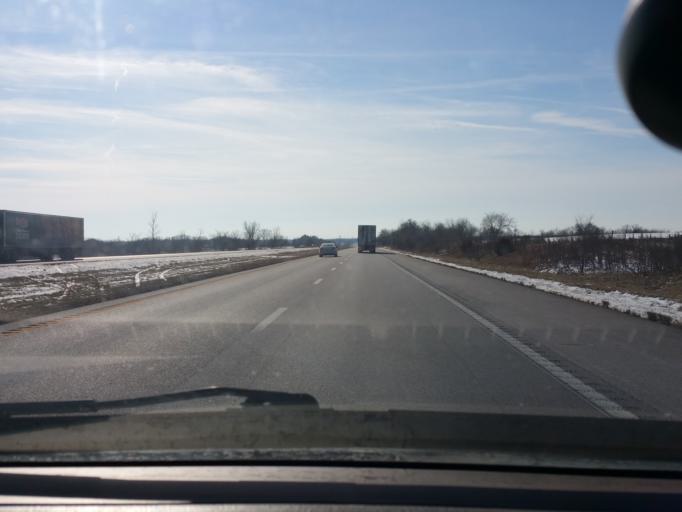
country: US
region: Missouri
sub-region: Clinton County
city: Cameron
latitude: 39.7853
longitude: -94.2072
